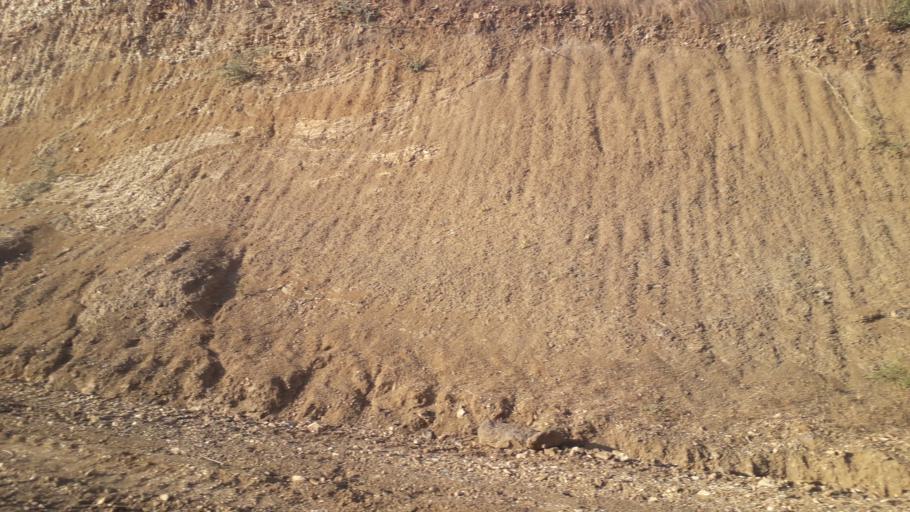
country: ET
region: Amhara
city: Dese
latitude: 11.5184
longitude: 39.2477
